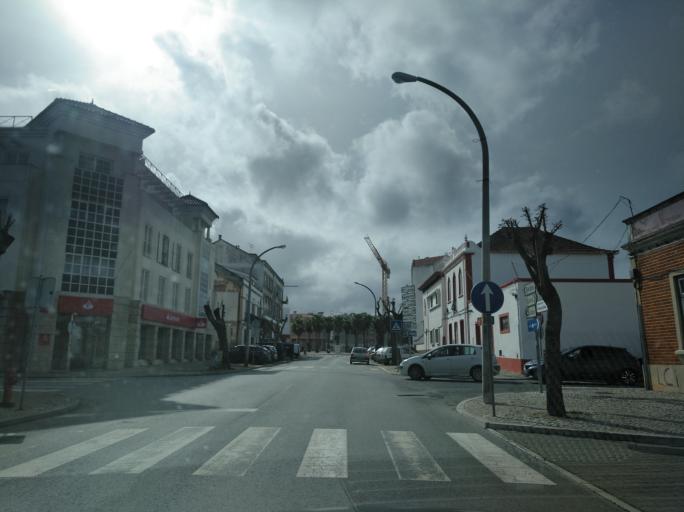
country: PT
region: Setubal
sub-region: Grandola
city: Grandola
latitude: 38.1771
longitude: -8.5658
